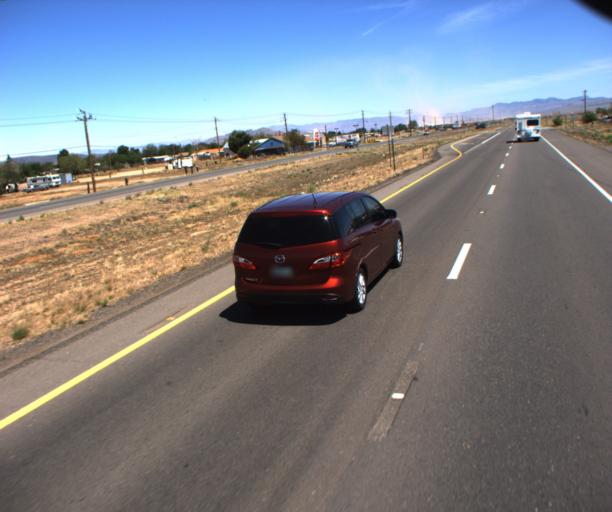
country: US
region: Arizona
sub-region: Mohave County
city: New Kingman-Butler
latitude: 35.2525
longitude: -113.9766
